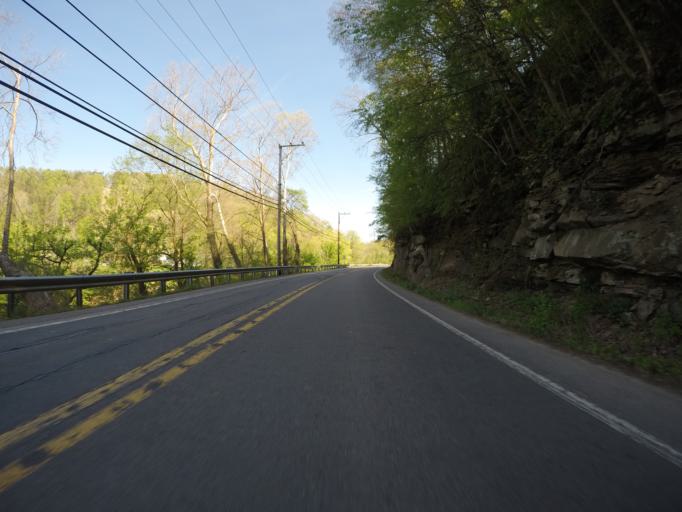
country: US
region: West Virginia
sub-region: Kanawha County
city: Clendenin
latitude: 38.4926
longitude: -81.3524
